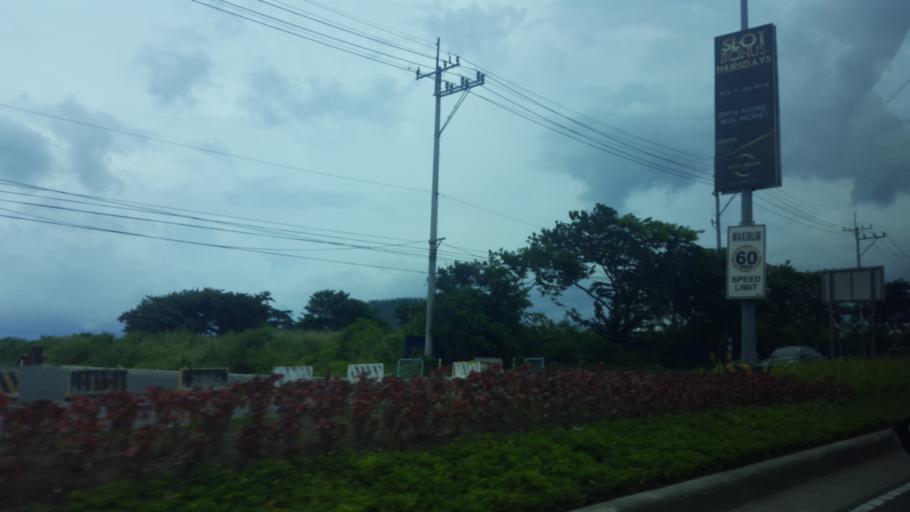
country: PH
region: Metro Manila
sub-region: Makati City
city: Makati City
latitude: 14.5263
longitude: 120.9899
